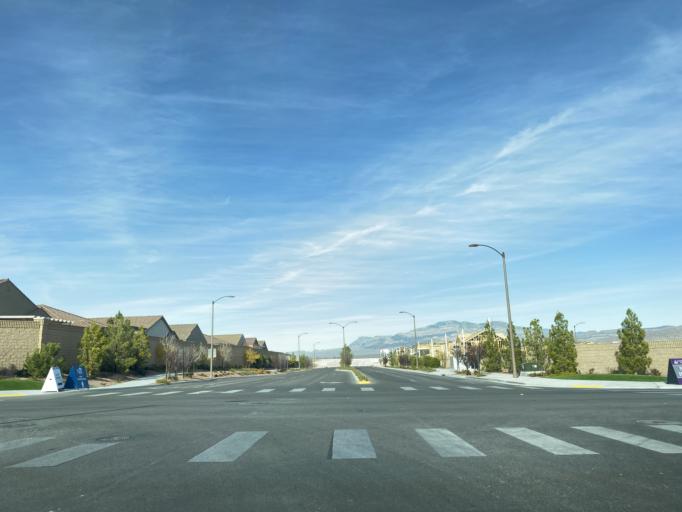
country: US
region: Nevada
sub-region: Clark County
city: Summerlin South
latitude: 36.3105
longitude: -115.3213
